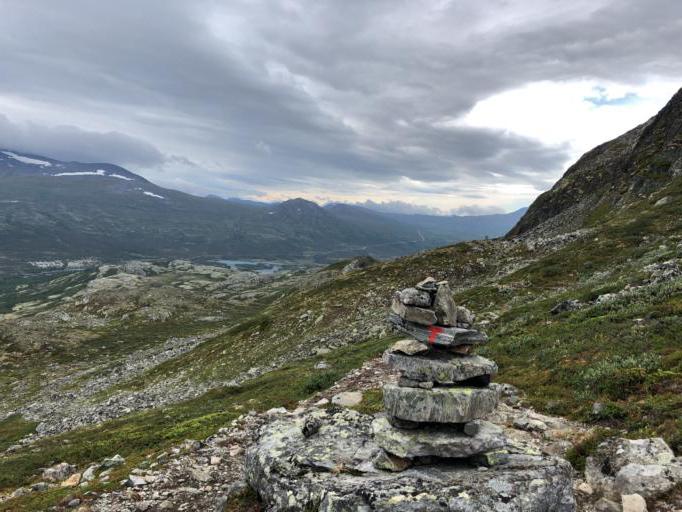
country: NO
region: Oppland
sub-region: Lom
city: Fossbergom
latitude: 61.5143
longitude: 8.8150
